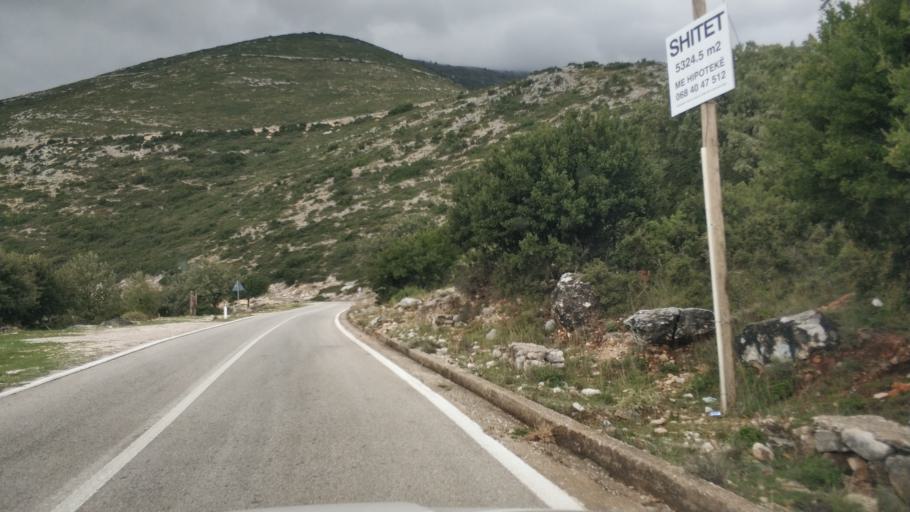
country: AL
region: Vlore
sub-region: Rrethi i Vlores
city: Vranisht
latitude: 40.1754
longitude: 19.6053
